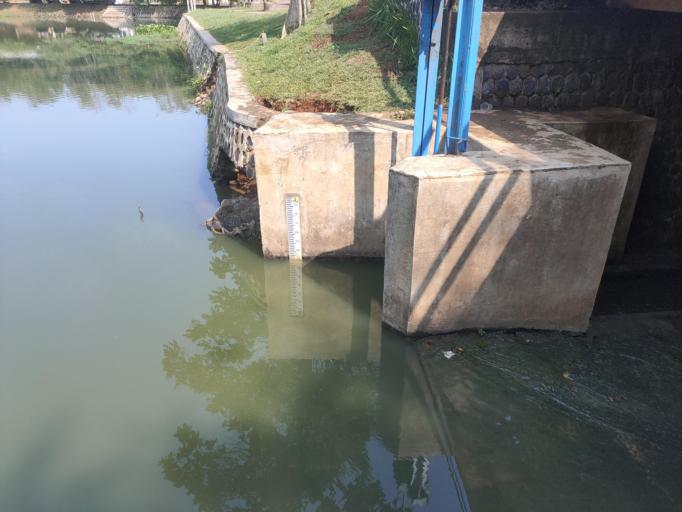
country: ID
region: West Java
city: Ciampea
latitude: -6.4828
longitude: 106.6605
